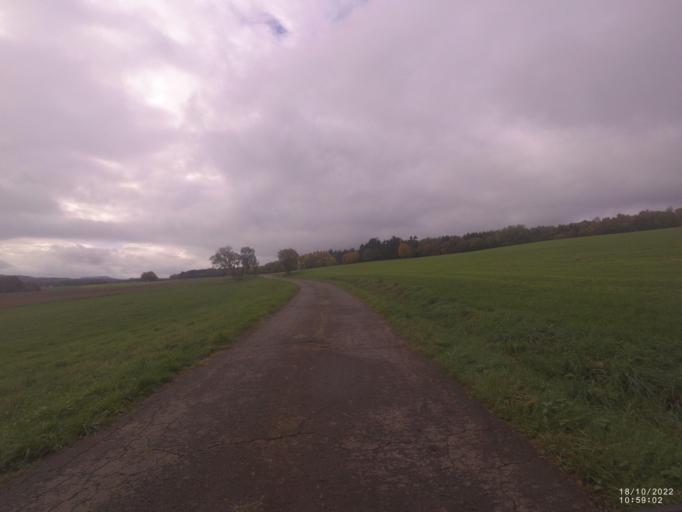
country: DE
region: Rheinland-Pfalz
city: Sarmersbach
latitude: 50.2262
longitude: 6.8874
